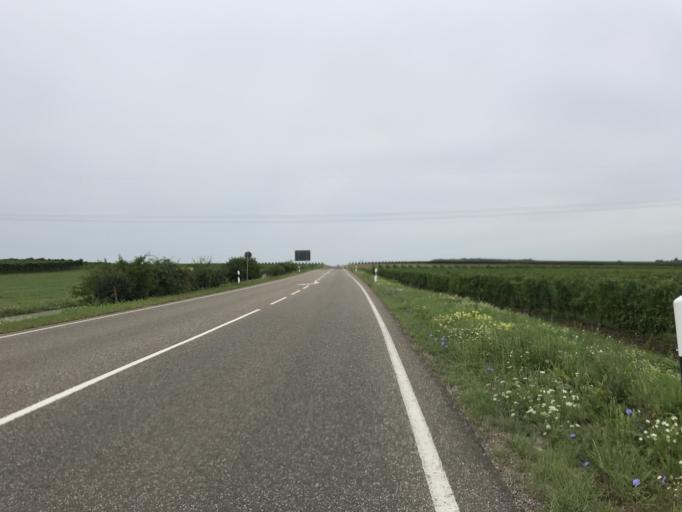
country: DE
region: Rheinland-Pfalz
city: Zotzenheim
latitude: 49.8610
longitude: 7.9634
